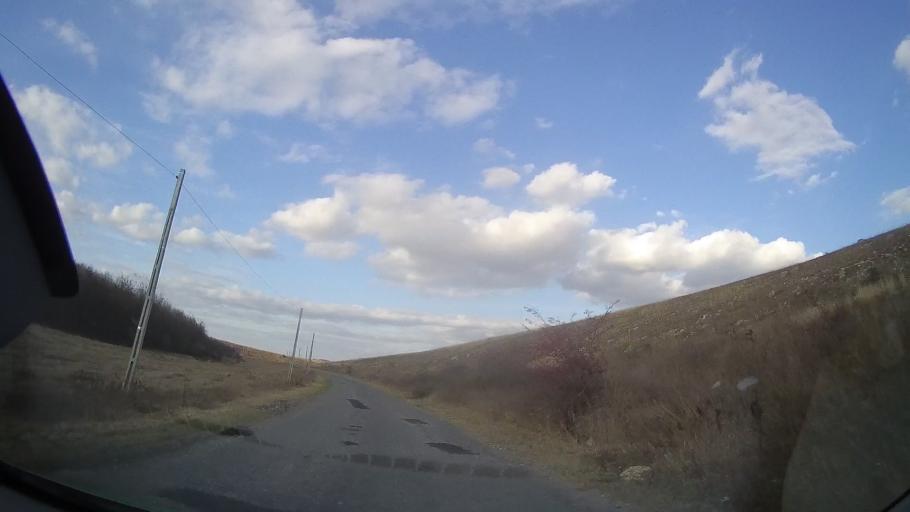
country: RO
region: Constanta
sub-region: Comuna Cerchezu
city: Cerchezu
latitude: 43.8348
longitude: 28.0974
